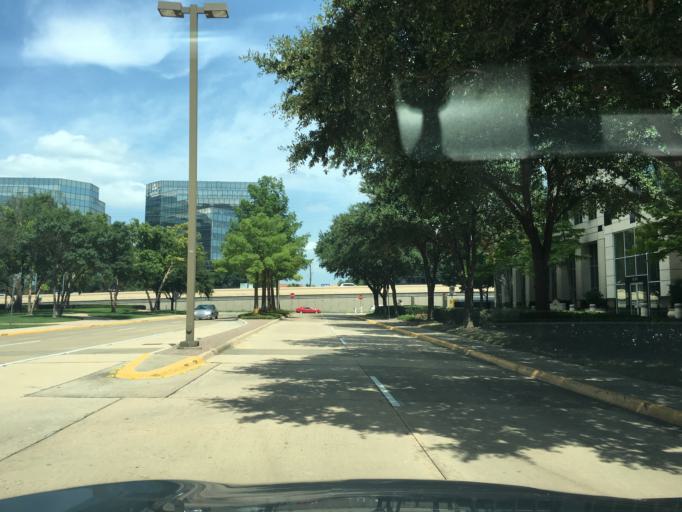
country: US
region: Texas
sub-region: Dallas County
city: Addison
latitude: 32.9409
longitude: -96.8235
